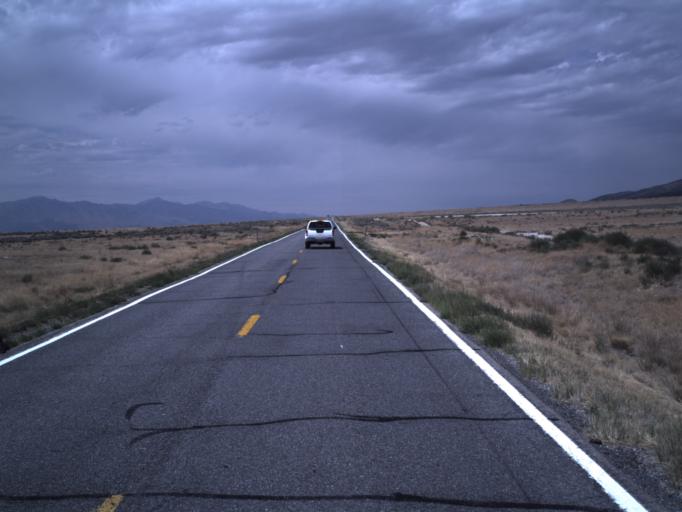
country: US
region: Utah
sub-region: Utah County
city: Eagle Mountain
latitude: 40.2451
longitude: -112.2108
